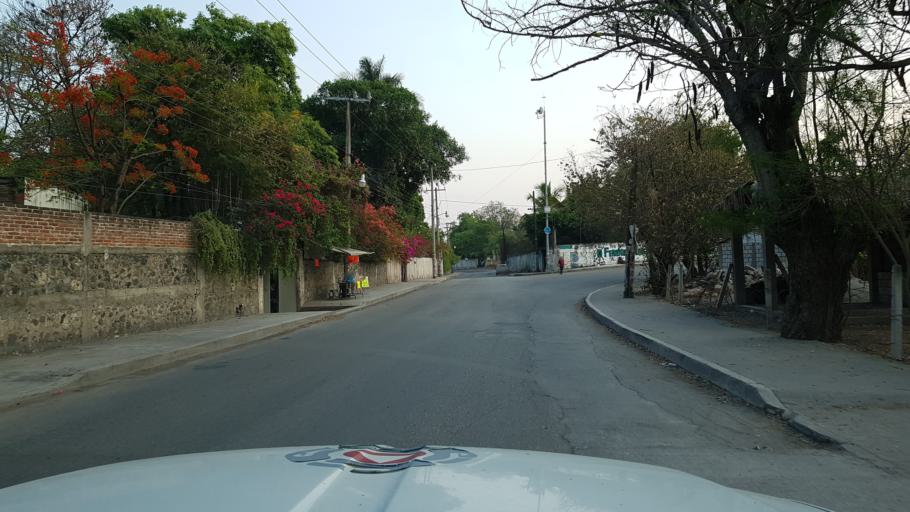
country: MX
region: Morelos
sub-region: Ayala
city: Abelardo L. Rodriguez
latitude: 18.7237
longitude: -98.9921
